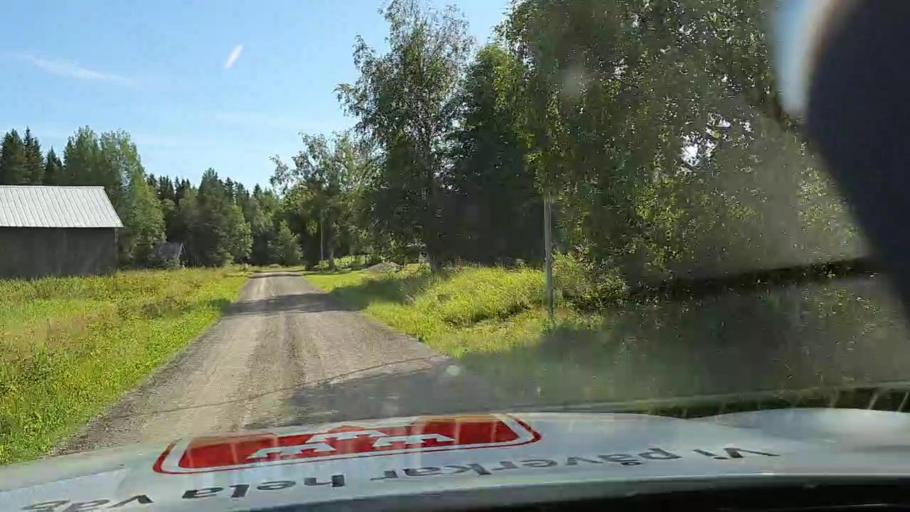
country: SE
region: Jaemtland
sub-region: Stroemsunds Kommun
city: Stroemsund
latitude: 63.7747
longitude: 15.3208
